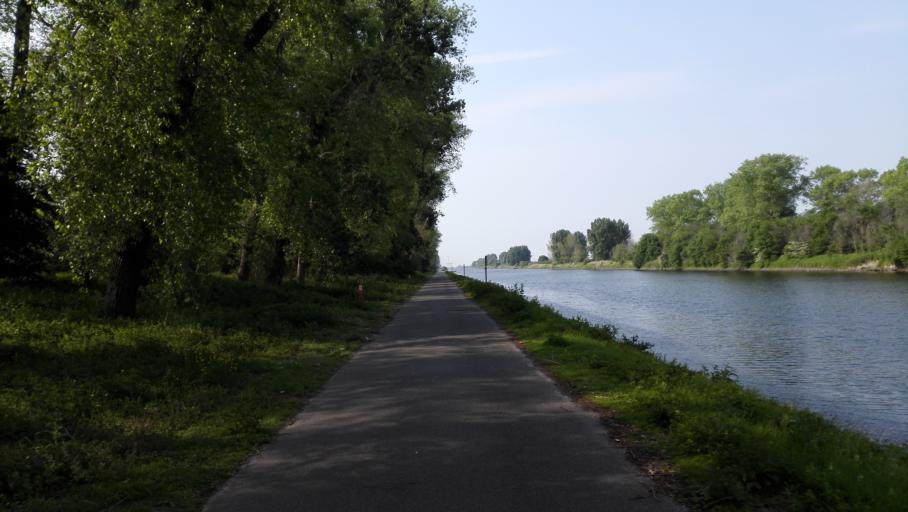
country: BE
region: Flanders
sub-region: Provincie West-Vlaanderen
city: Zeebrugge
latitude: 51.2874
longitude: 3.2079
